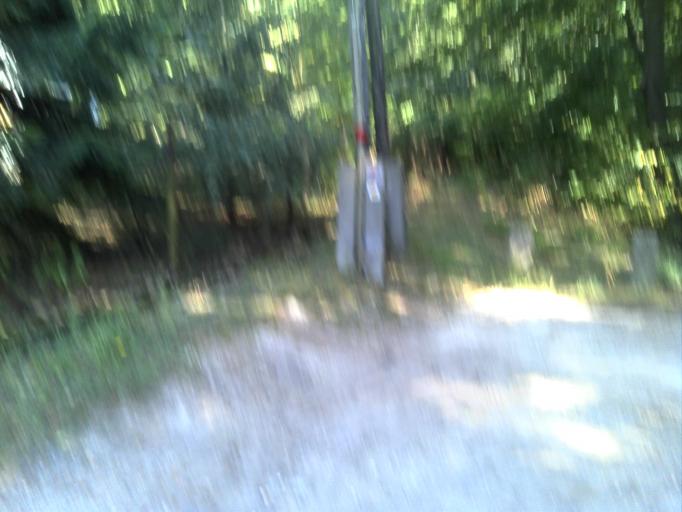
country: HU
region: Pest
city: Piliscsaba
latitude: 47.6354
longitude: 18.8549
